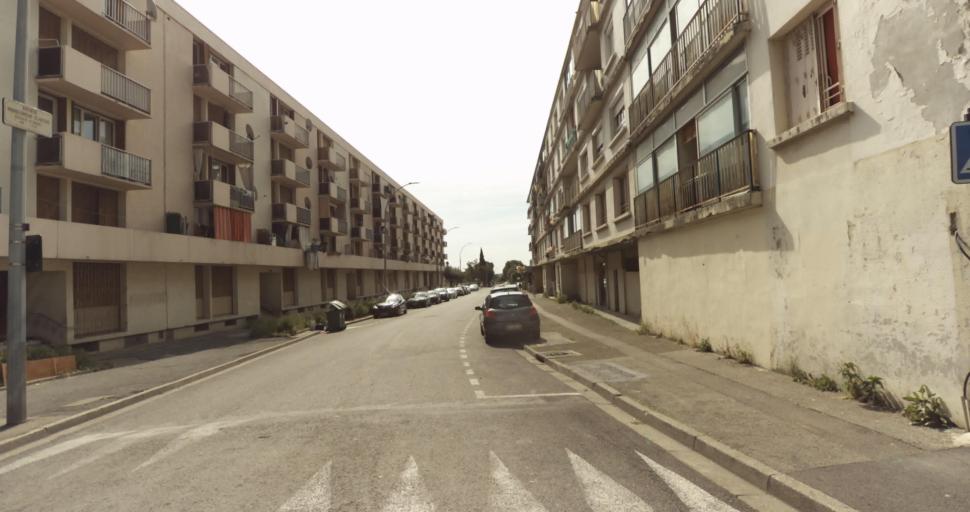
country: FR
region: Languedoc-Roussillon
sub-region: Departement du Gard
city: Rodilhan
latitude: 43.8558
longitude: 4.3981
